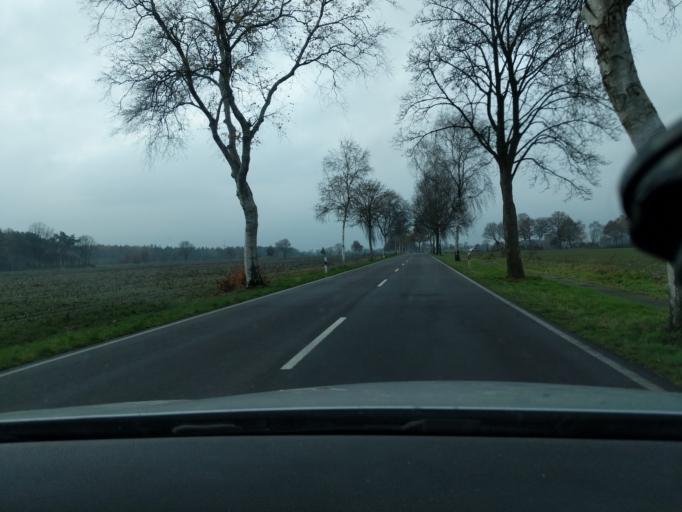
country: DE
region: Lower Saxony
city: Ahlerstedt
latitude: 53.3759
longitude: 9.4567
